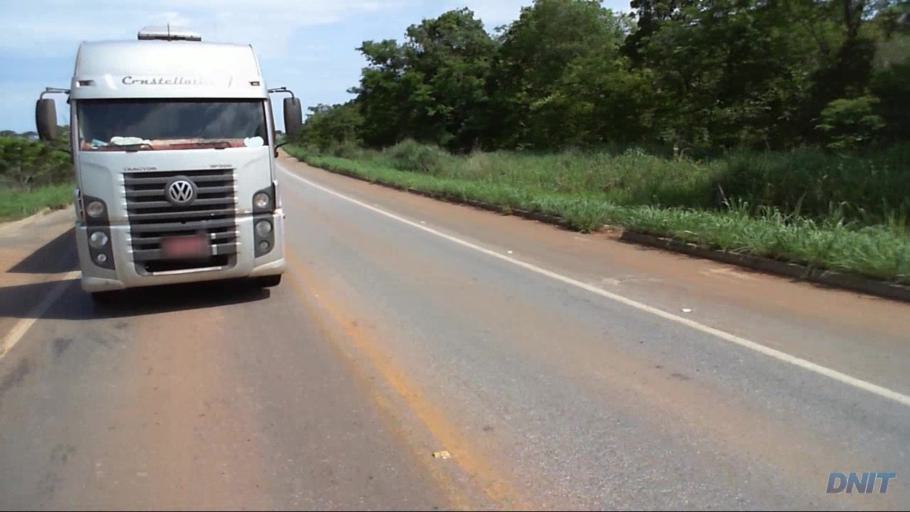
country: BR
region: Goias
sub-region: Barro Alto
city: Barro Alto
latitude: -15.1295
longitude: -48.8348
